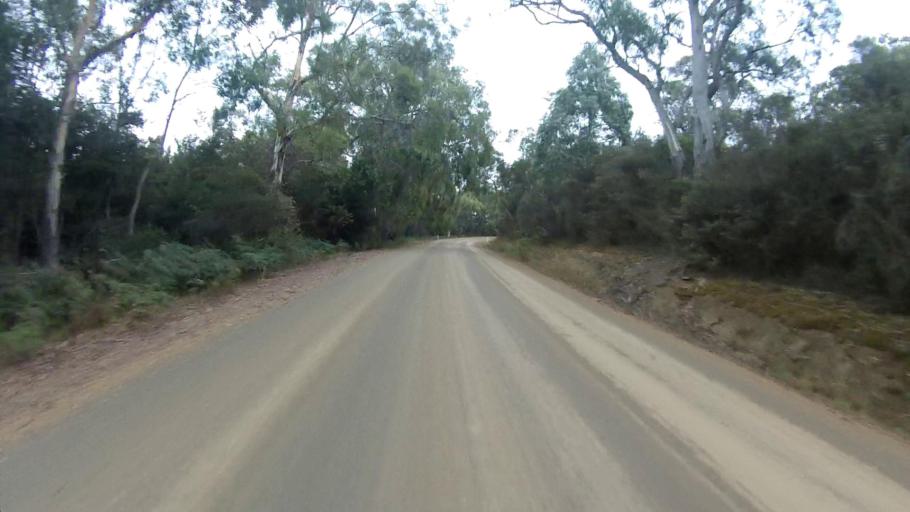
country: AU
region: Tasmania
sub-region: Huon Valley
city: Cygnet
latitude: -43.2247
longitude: 147.0956
